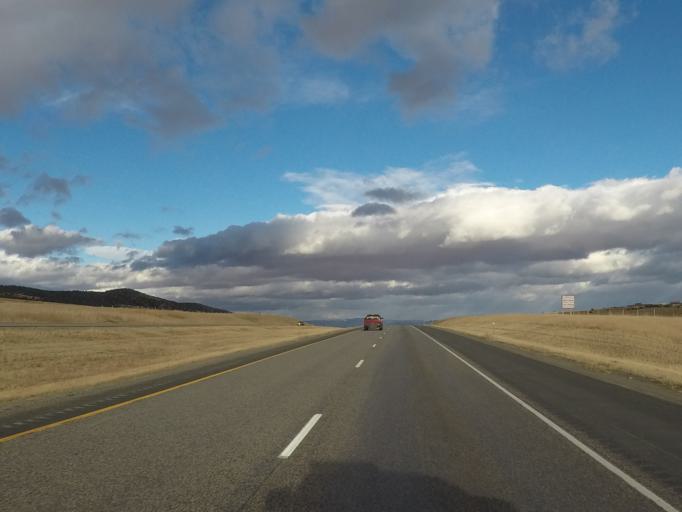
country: US
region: Montana
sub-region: Jefferson County
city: Whitehall
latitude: 45.8892
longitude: -111.8588
